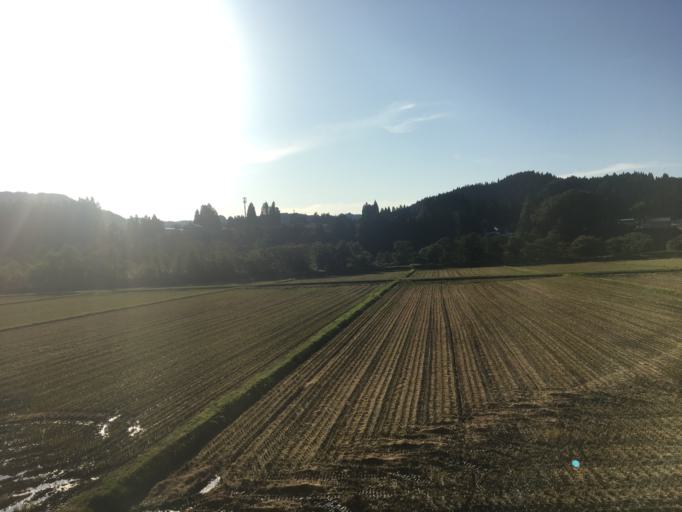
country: JP
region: Akita
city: Takanosu
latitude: 40.0298
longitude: 140.4004
